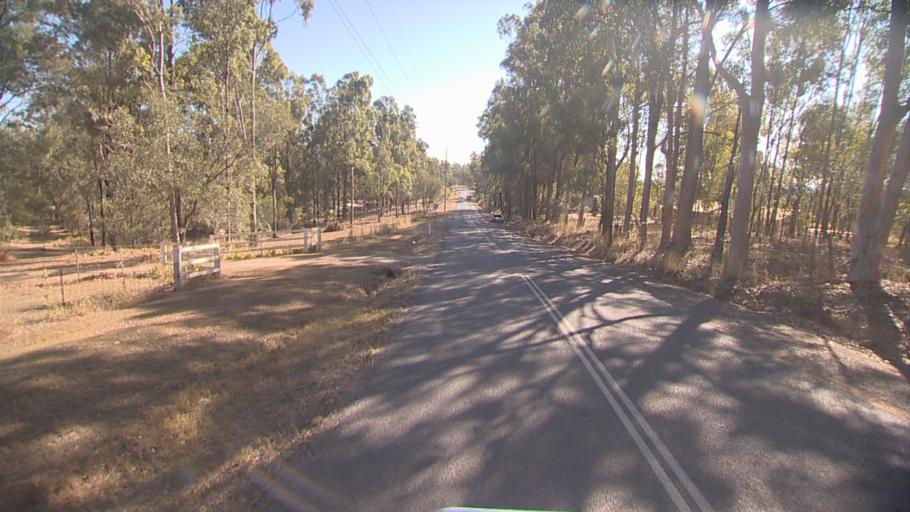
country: AU
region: Queensland
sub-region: Logan
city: Cedar Vale
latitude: -27.8853
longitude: 153.0176
